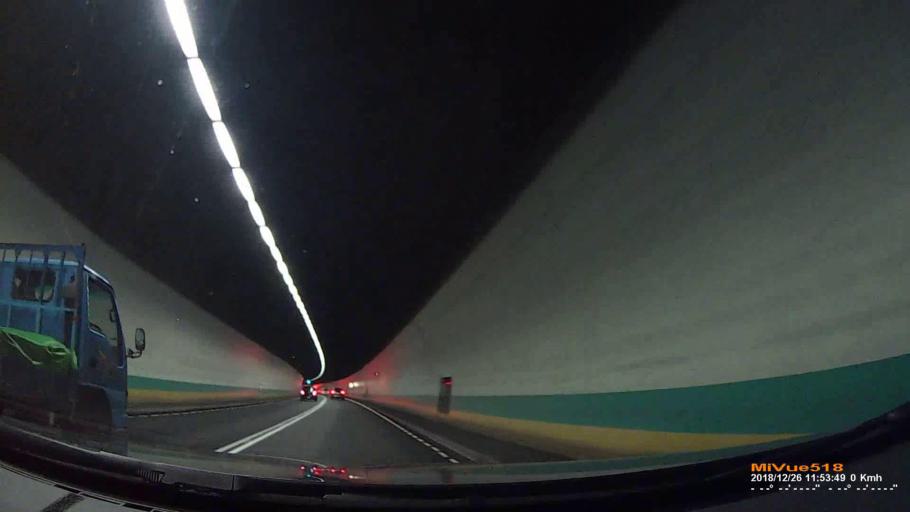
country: TW
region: Taiwan
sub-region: Keelung
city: Keelung
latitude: 24.9553
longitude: 121.6955
